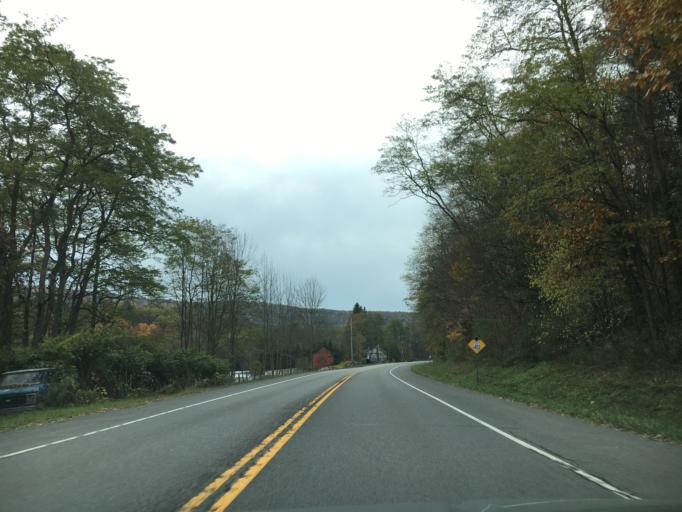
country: US
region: New York
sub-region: Otsego County
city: Oneonta
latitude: 42.5382
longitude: -74.9627
